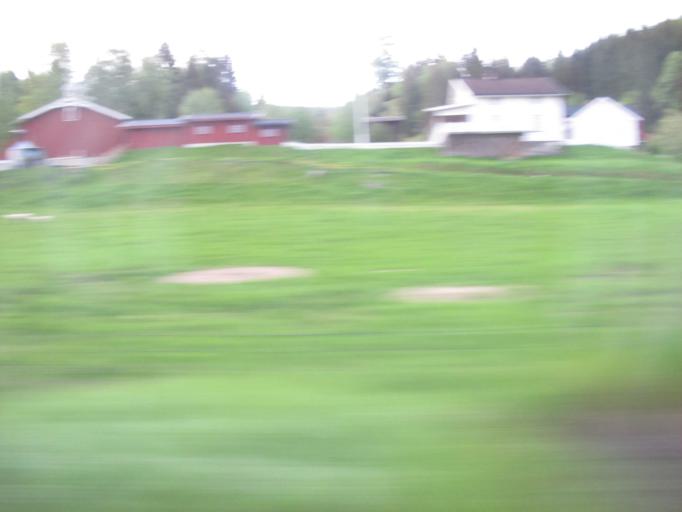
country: NO
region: Oppland
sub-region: Lillehammer
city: Lillehammer
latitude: 61.0879
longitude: 10.4638
